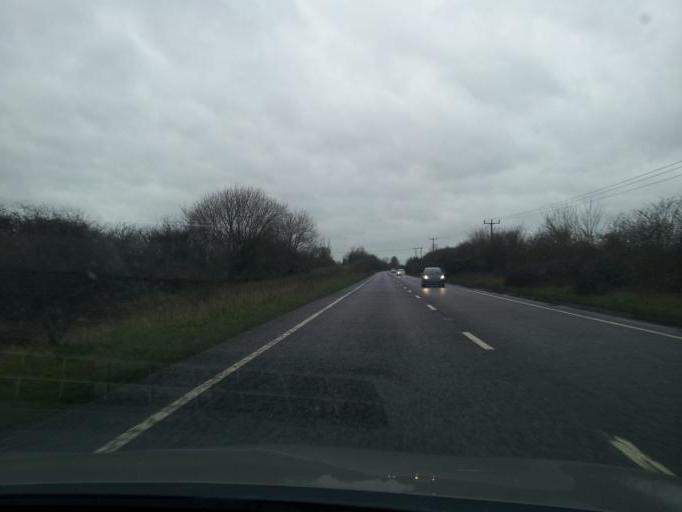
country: GB
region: England
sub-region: Suffolk
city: Botesdale
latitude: 52.3354
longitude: 1.0047
